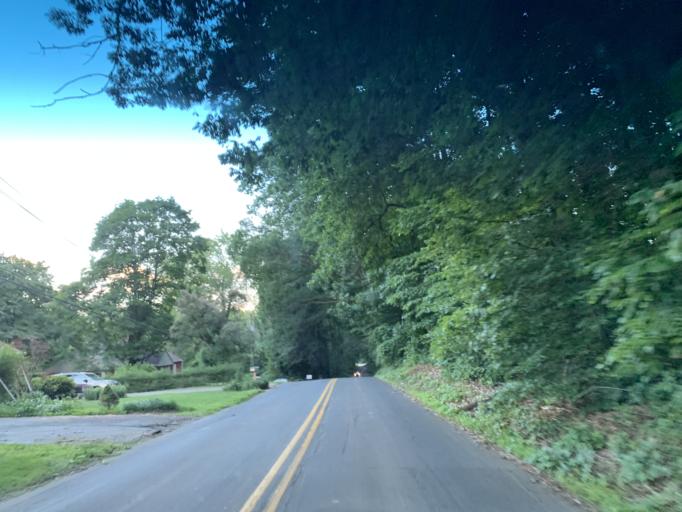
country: US
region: Maryland
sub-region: Harford County
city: Aberdeen
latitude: 39.5320
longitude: -76.1477
